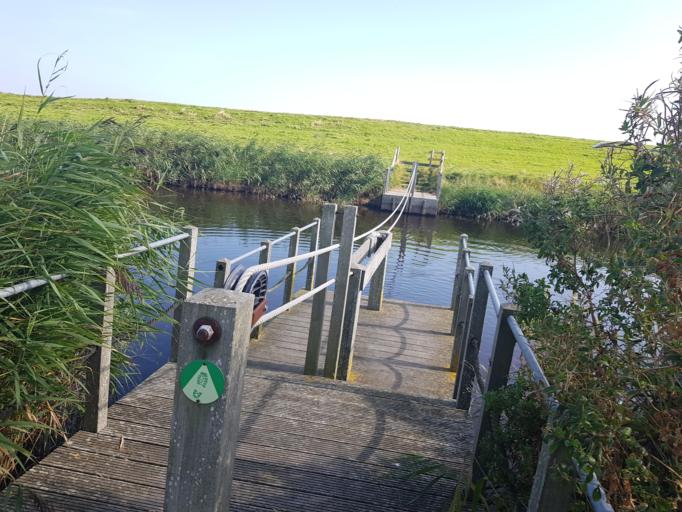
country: NL
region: North Holland
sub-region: Gemeente Texel
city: Den Burg
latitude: 53.1063
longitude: 4.8600
